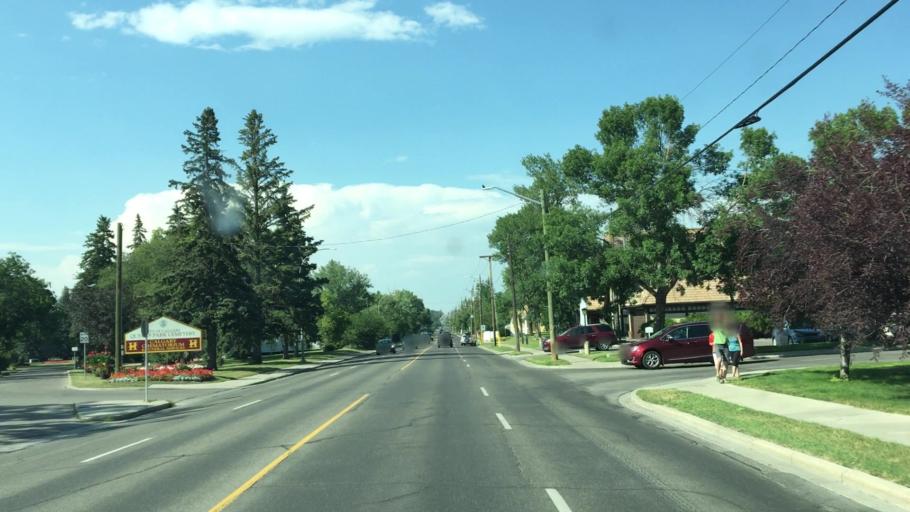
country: CA
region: Alberta
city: Calgary
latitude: 51.0803
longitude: -114.0715
